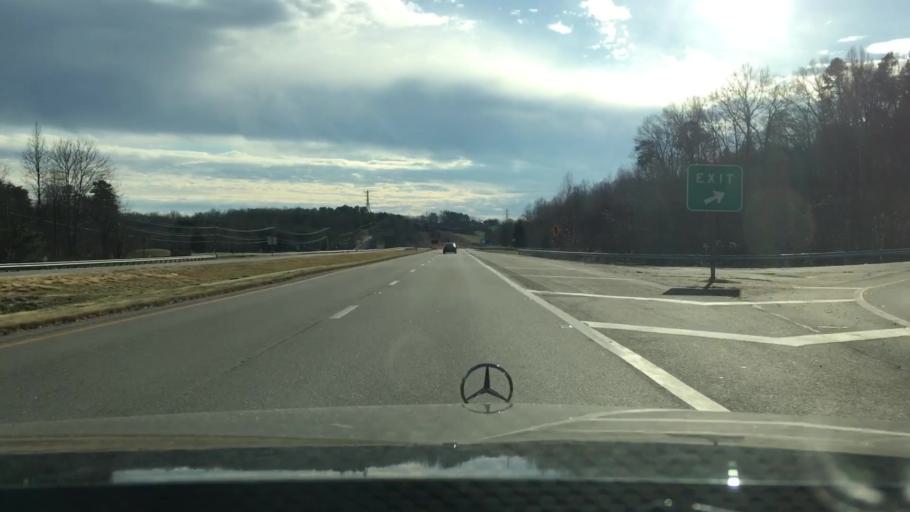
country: US
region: Virginia
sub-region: City of Danville
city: Danville
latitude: 36.5834
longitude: -79.3596
